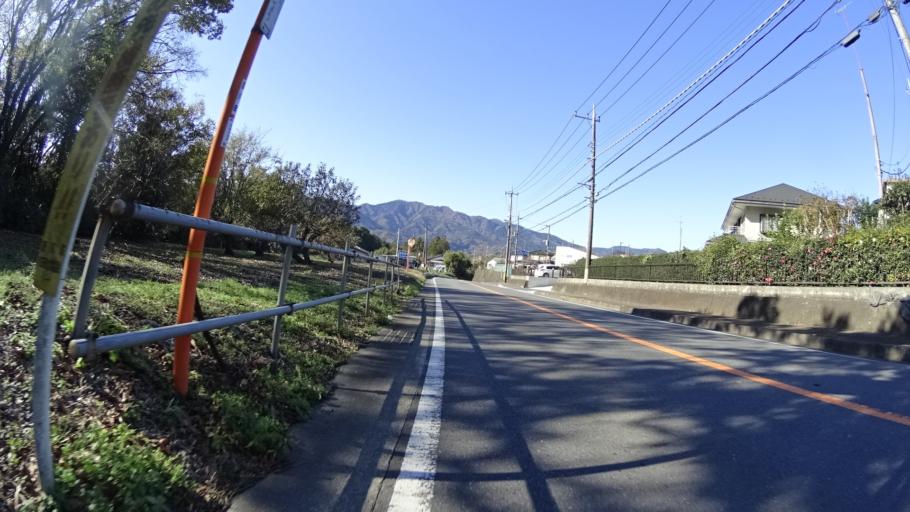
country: JP
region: Kanagawa
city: Zama
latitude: 35.5294
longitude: 139.3179
